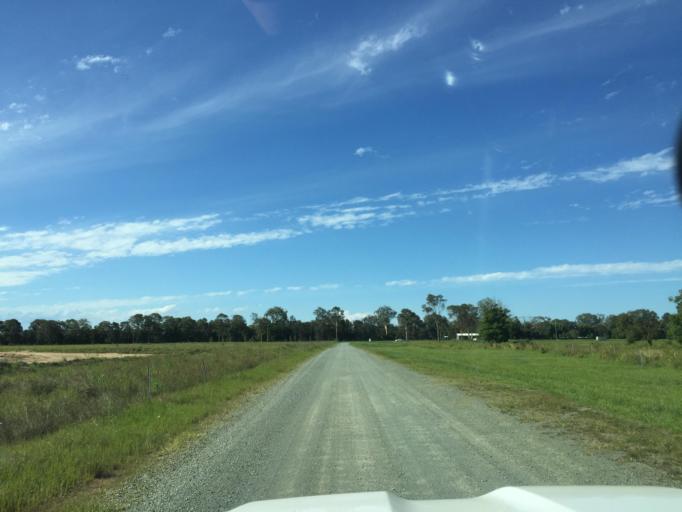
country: AU
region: Queensland
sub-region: Moreton Bay
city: Morayfield
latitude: -27.1100
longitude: 152.9930
